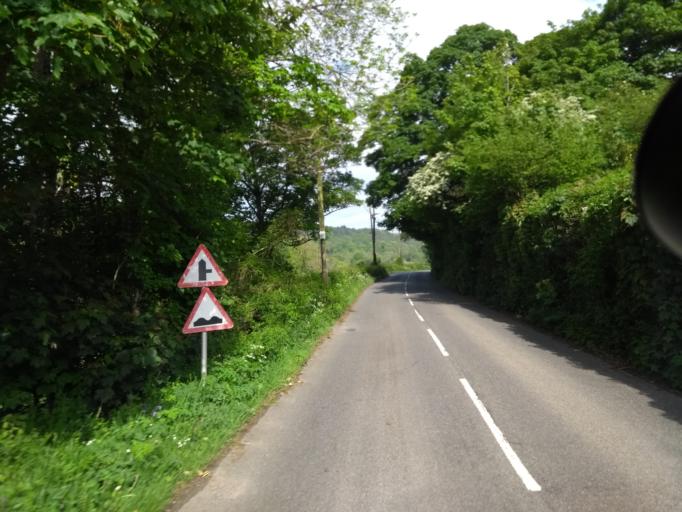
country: GB
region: England
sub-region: Dorset
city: Lyme Regis
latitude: 50.7390
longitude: -2.9631
